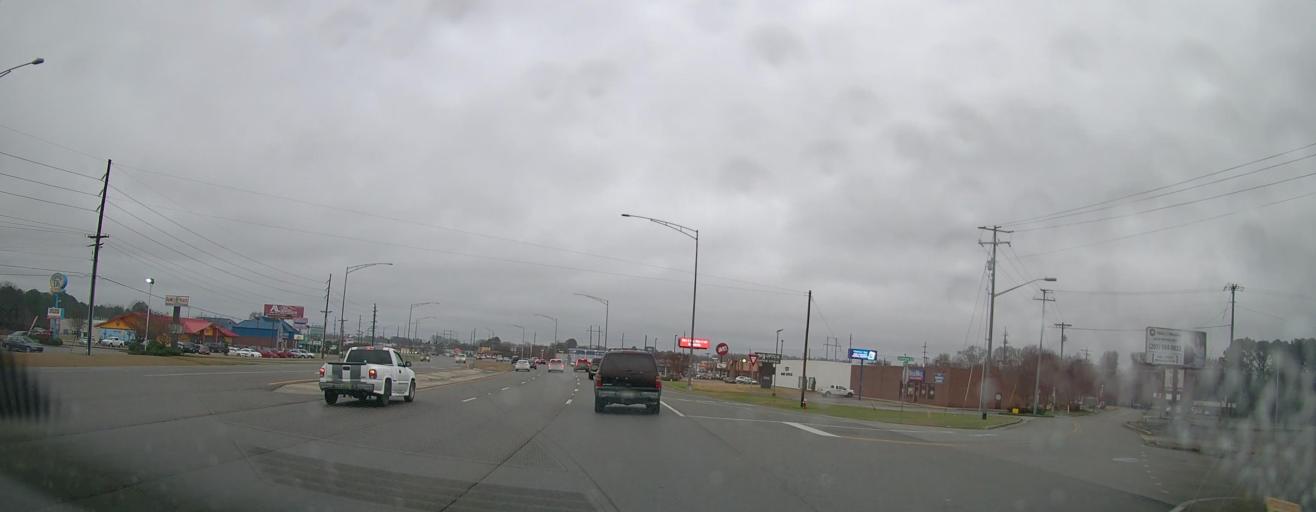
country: US
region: Alabama
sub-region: Morgan County
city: Decatur
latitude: 34.5629
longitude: -87.0089
